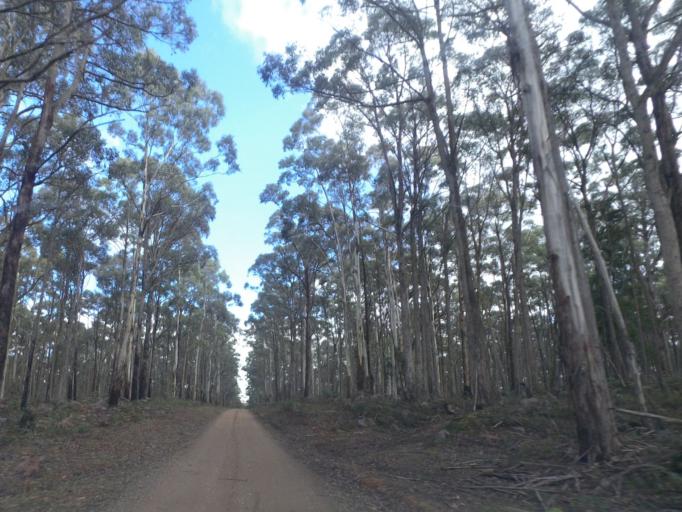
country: AU
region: Victoria
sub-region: Moorabool
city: Bacchus Marsh
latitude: -37.4368
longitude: 144.4622
